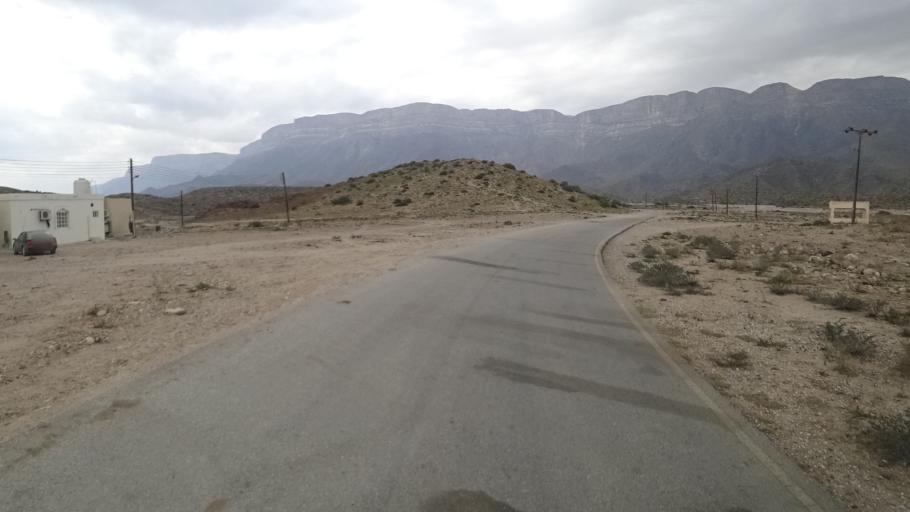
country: OM
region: Zufar
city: Salalah
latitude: 17.1664
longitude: 54.9782
